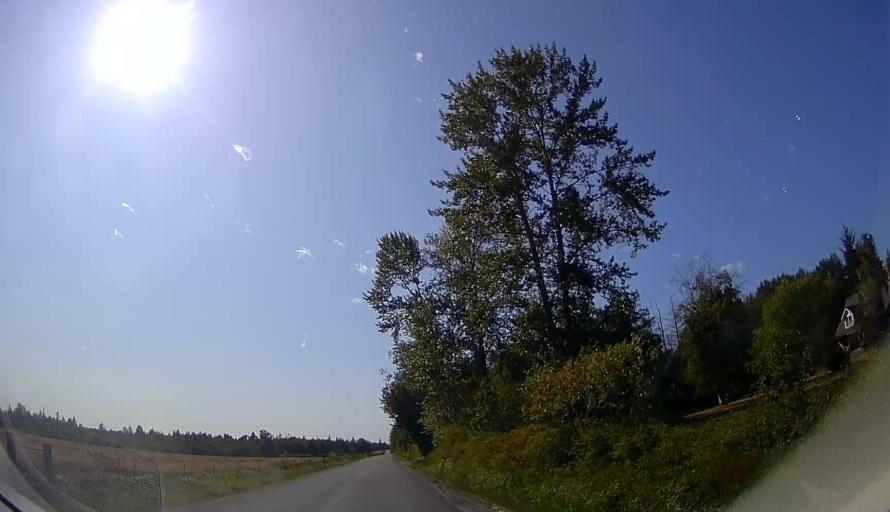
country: US
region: Washington
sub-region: Skagit County
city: Burlington
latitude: 48.4939
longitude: -122.4487
